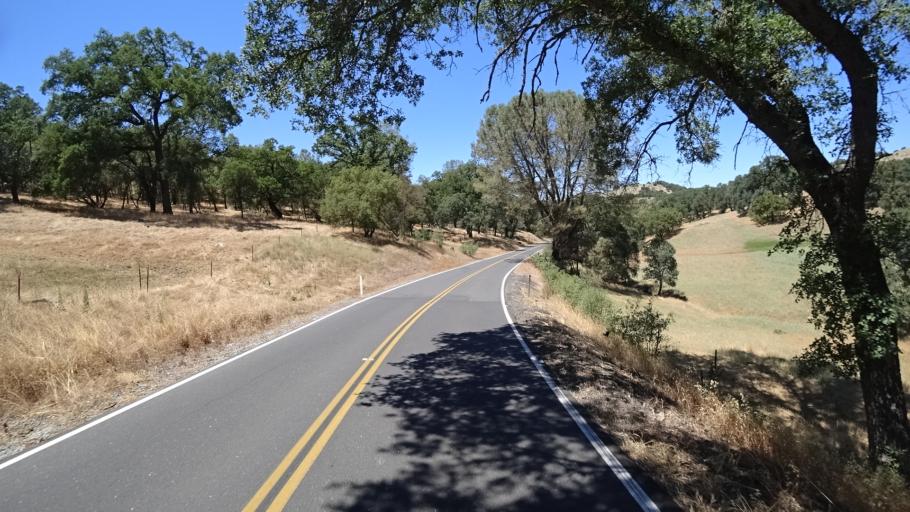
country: US
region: California
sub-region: Calaveras County
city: San Andreas
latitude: 38.1519
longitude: -120.6618
